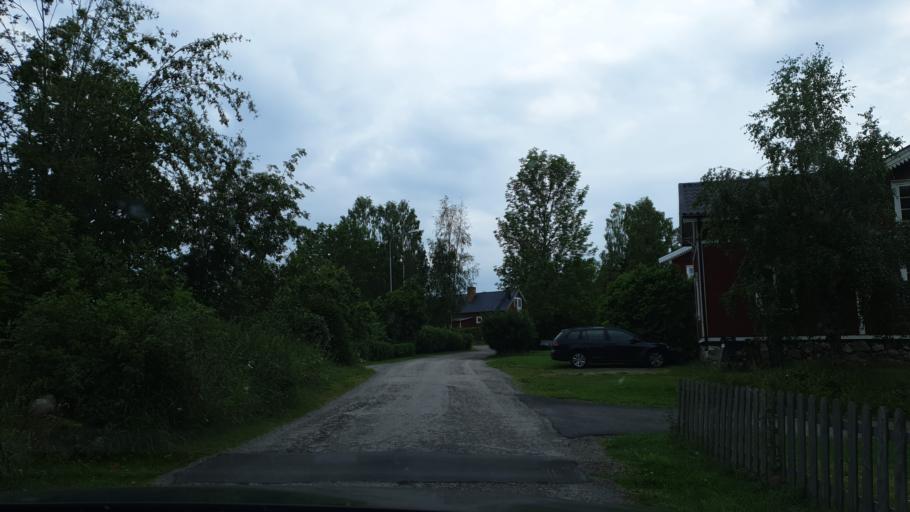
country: SE
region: Gaevleborg
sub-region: Hudiksvalls Kommun
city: Iggesund
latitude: 61.5425
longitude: 17.0054
